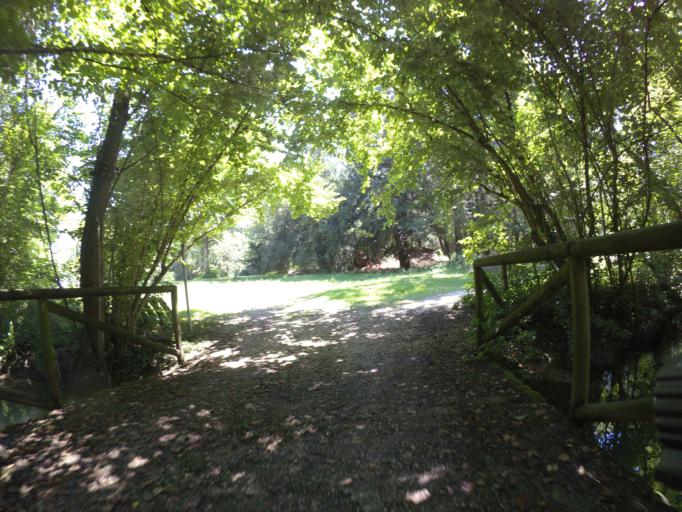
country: IT
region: Friuli Venezia Giulia
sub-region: Provincia di Udine
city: Teor
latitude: 45.8738
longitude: 13.0812
